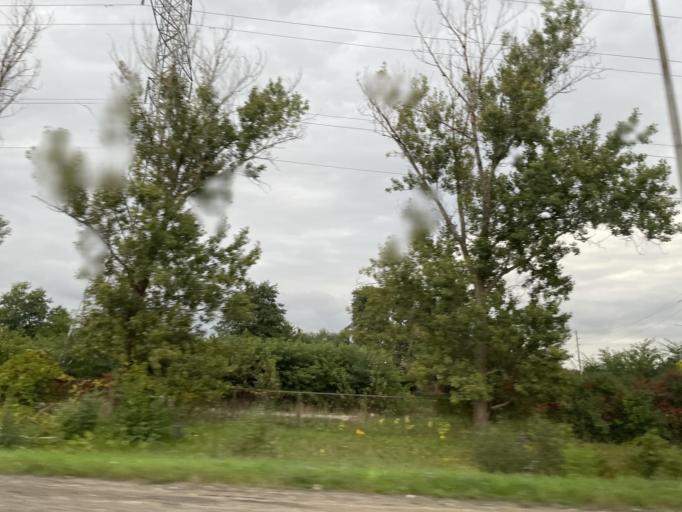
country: CA
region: Ontario
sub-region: Wellington County
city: Guelph
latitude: 43.5348
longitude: -80.2765
